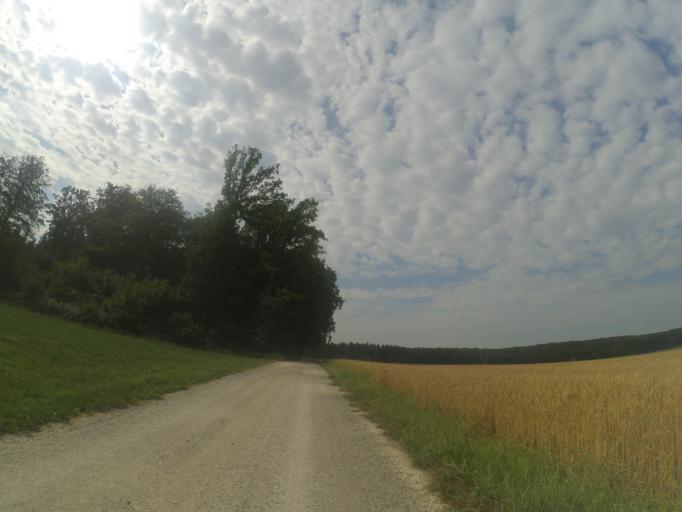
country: DE
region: Baden-Wuerttemberg
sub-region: Tuebingen Region
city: Lonsee
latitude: 48.5133
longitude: 9.8819
